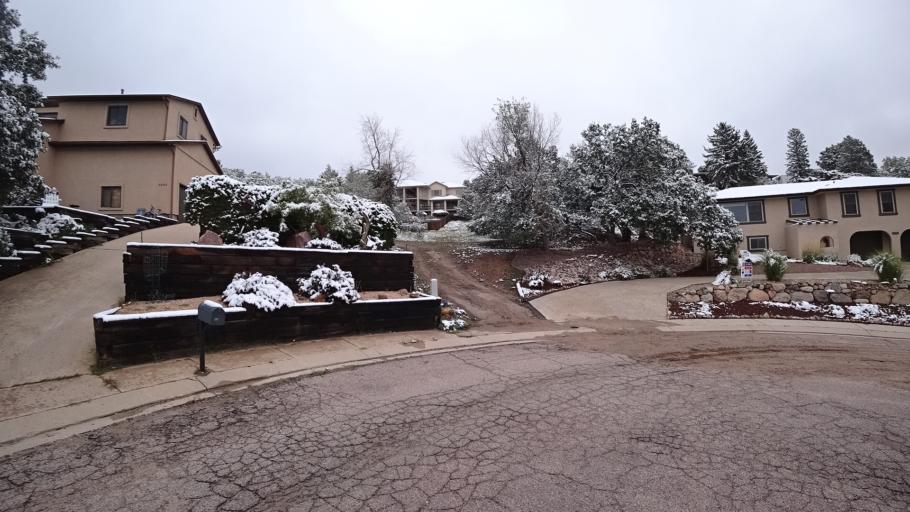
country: US
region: Colorado
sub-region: El Paso County
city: Cimarron Hills
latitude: 38.9129
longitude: -104.7621
